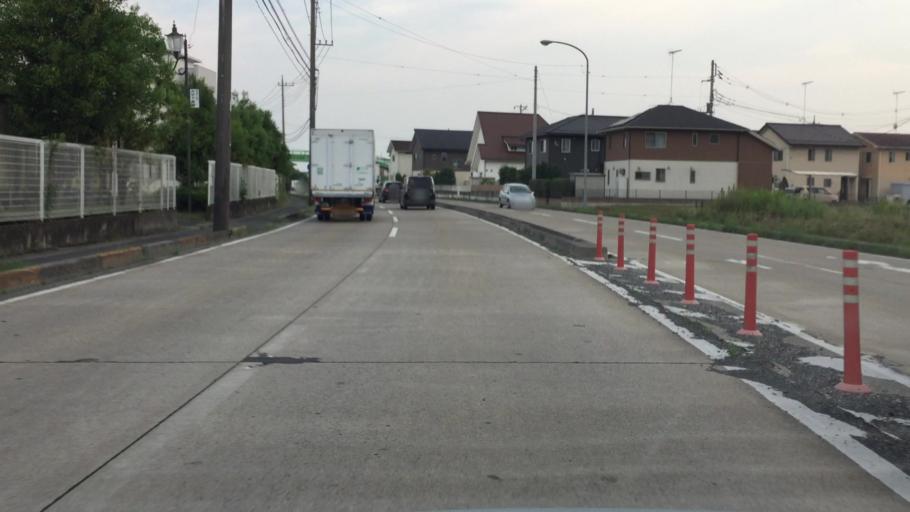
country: JP
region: Tochigi
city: Tochigi
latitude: 36.3433
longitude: 139.6975
